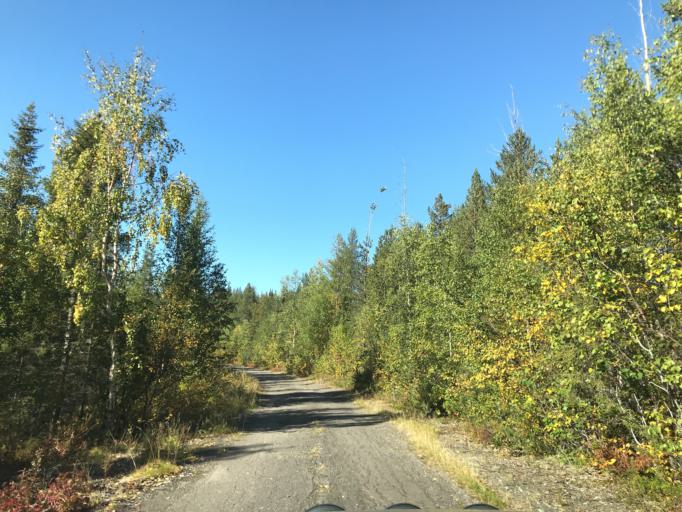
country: SE
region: Norrbotten
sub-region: Gallivare Kommun
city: Malmberget
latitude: 67.6467
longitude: 21.1021
